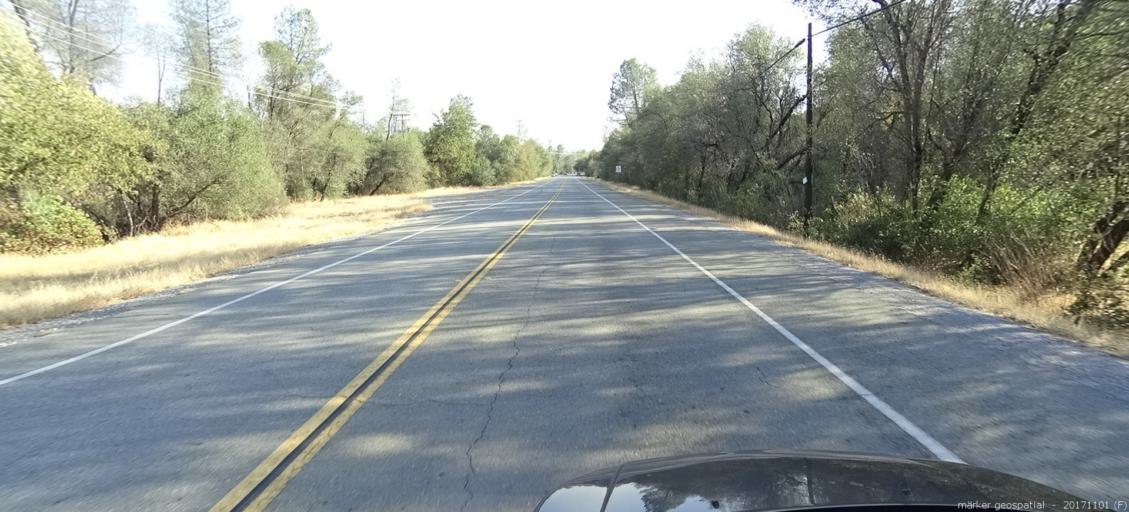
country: US
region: California
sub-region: Shasta County
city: Shasta Lake
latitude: 40.6283
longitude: -122.3234
